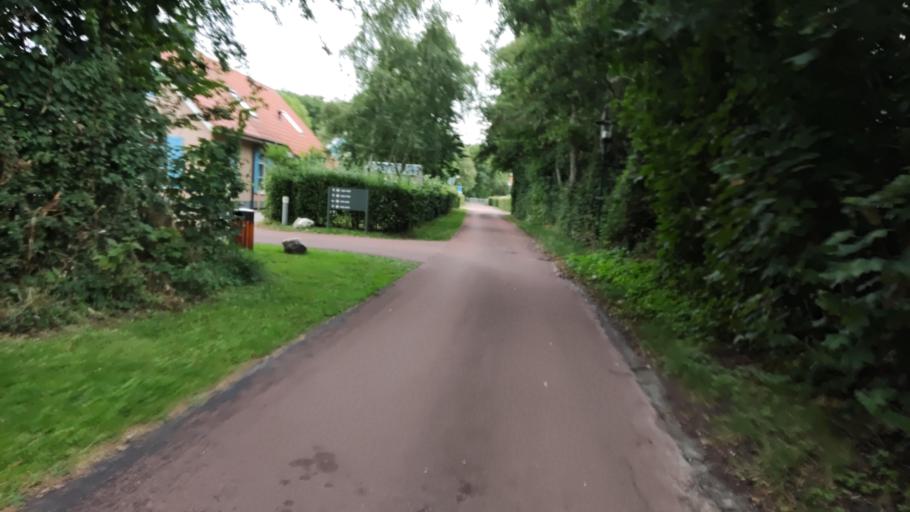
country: NL
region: North Holland
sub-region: Gemeente Texel
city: Den Burg
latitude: 53.0876
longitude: 4.7698
